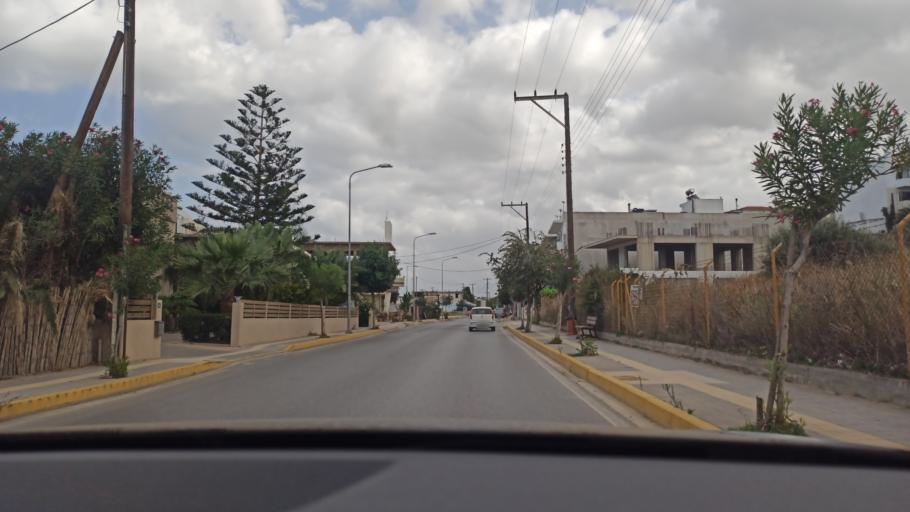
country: GR
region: Crete
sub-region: Nomos Irakleiou
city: Gazi
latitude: 35.3354
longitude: 25.0887
